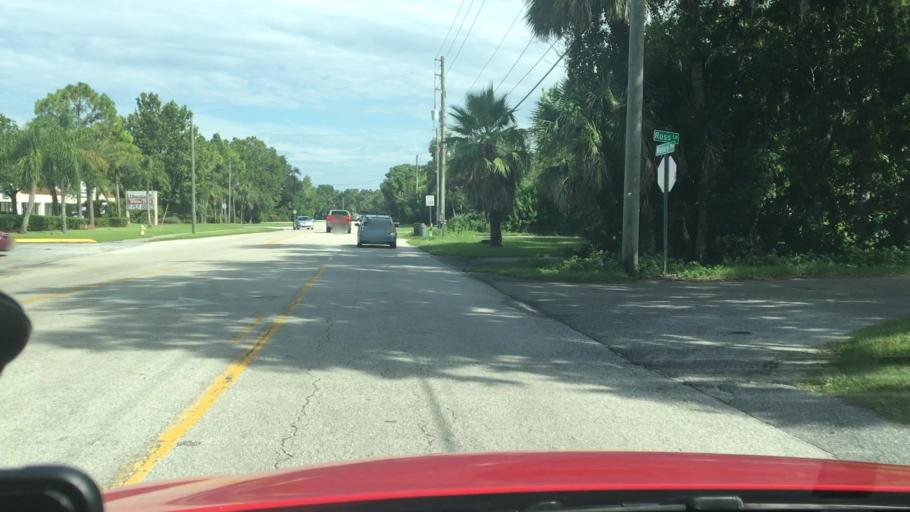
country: US
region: Florida
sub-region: Volusia County
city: New Smyrna Beach
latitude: 29.0154
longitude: -80.9422
